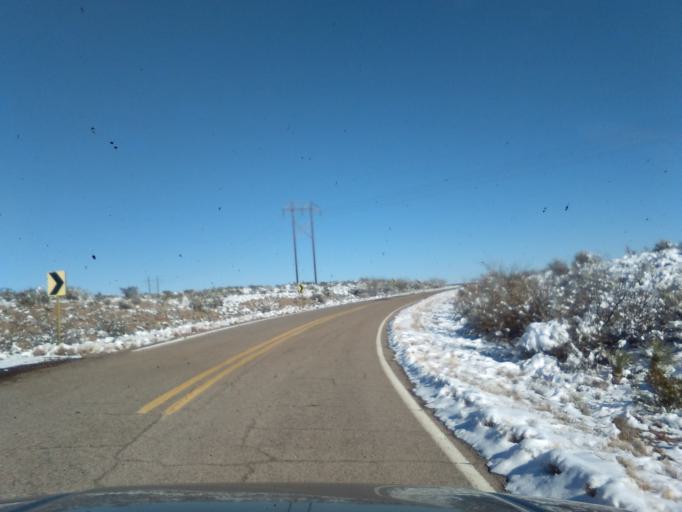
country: US
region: New Mexico
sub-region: Sierra County
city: Elephant Butte
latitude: 33.6194
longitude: -107.1401
